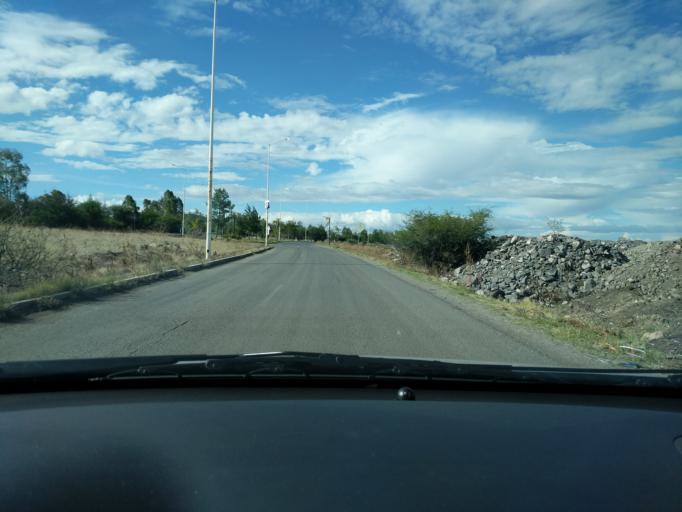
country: MX
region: Queretaro
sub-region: El Marques
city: Paseos del Marques
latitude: 20.5913
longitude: -100.2789
